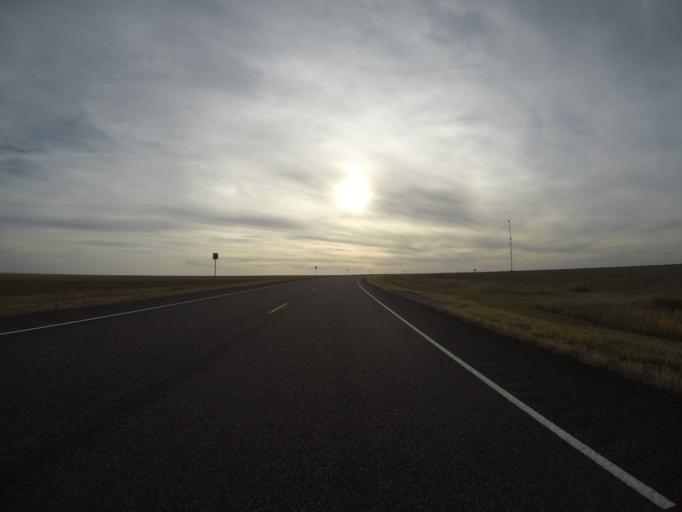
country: US
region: Kansas
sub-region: Cheyenne County
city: Saint Francis
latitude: 39.7479
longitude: -102.0574
